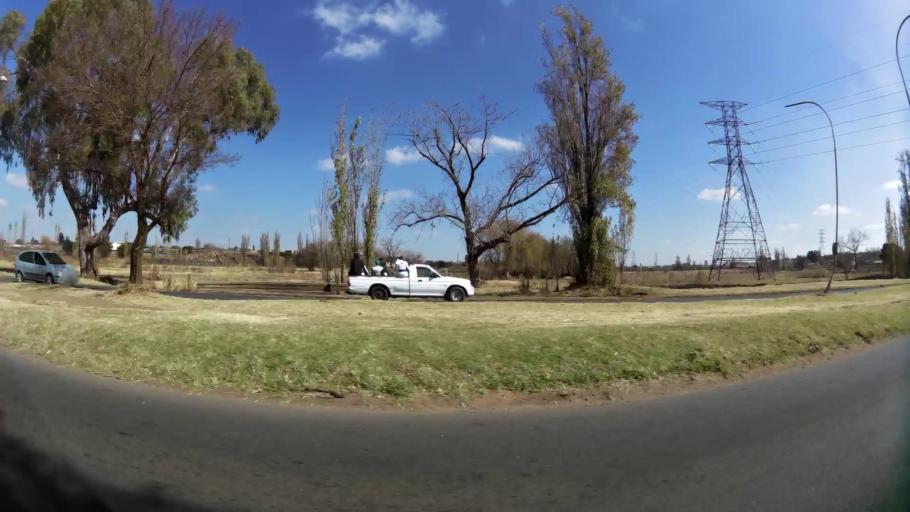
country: ZA
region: Gauteng
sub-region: City of Johannesburg Metropolitan Municipality
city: Soweto
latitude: -26.2399
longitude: 27.8792
